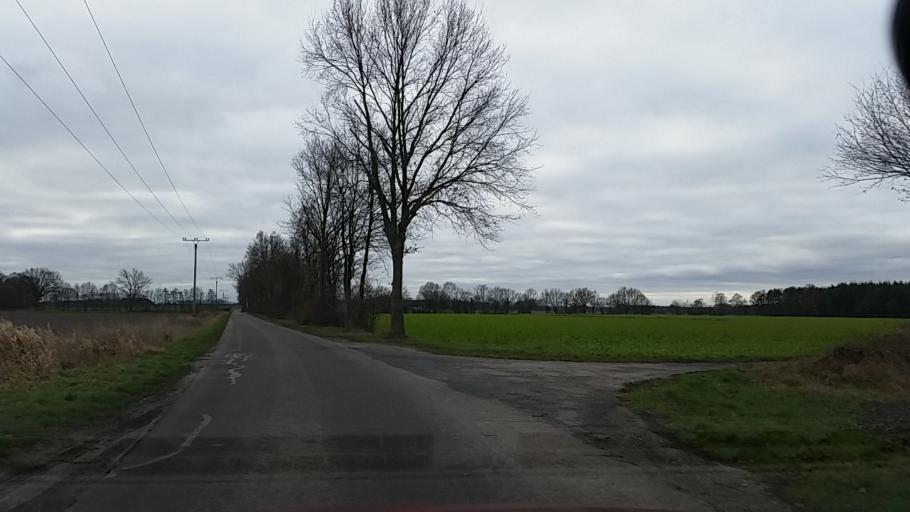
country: DE
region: Lower Saxony
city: Luder
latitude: 52.7622
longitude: 10.6848
